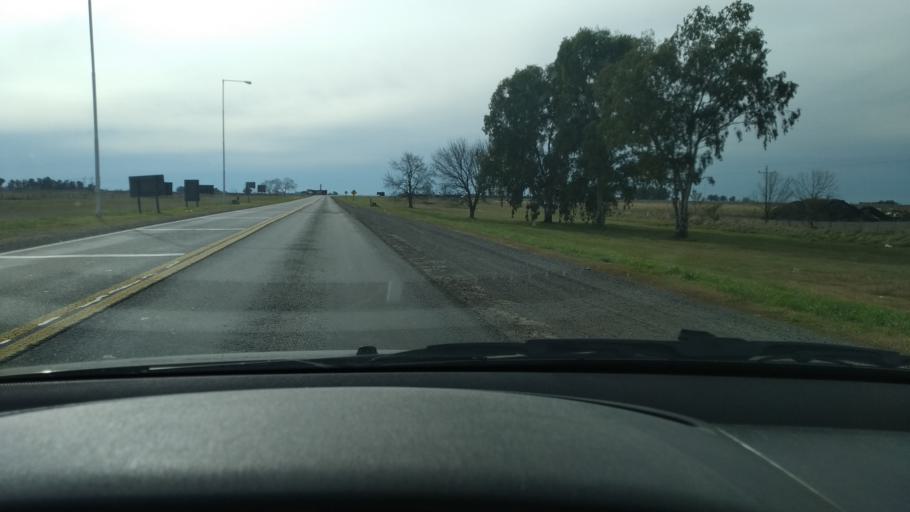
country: AR
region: Buenos Aires
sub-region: Partido de Azul
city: Azul
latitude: -36.7565
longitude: -59.8050
